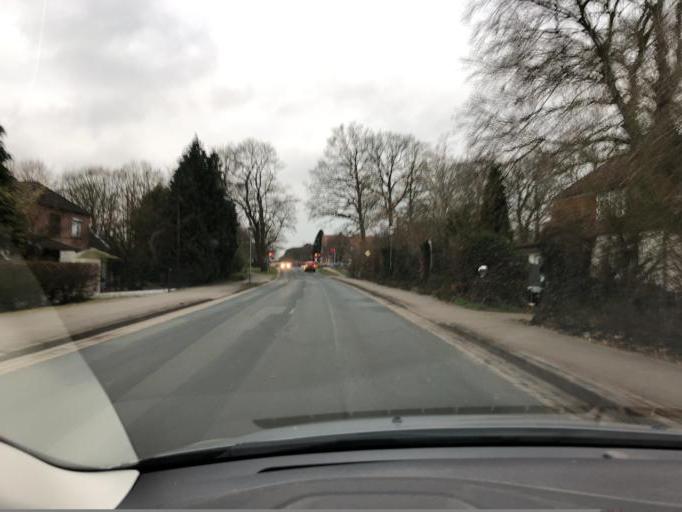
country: DE
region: Lower Saxony
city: Delmenhorst
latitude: 53.0854
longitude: 8.5807
